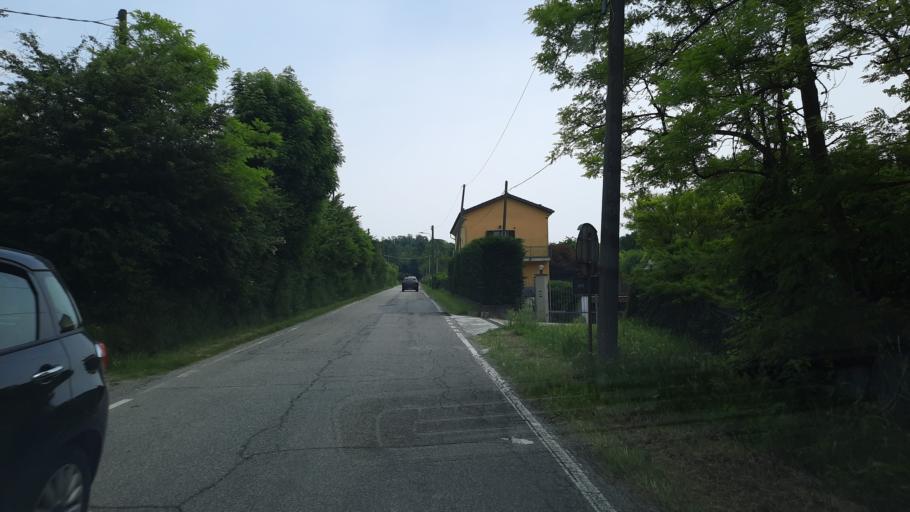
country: IT
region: Piedmont
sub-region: Provincia di Alessandria
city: Ozzano Monferrato
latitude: 45.1016
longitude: 8.3829
